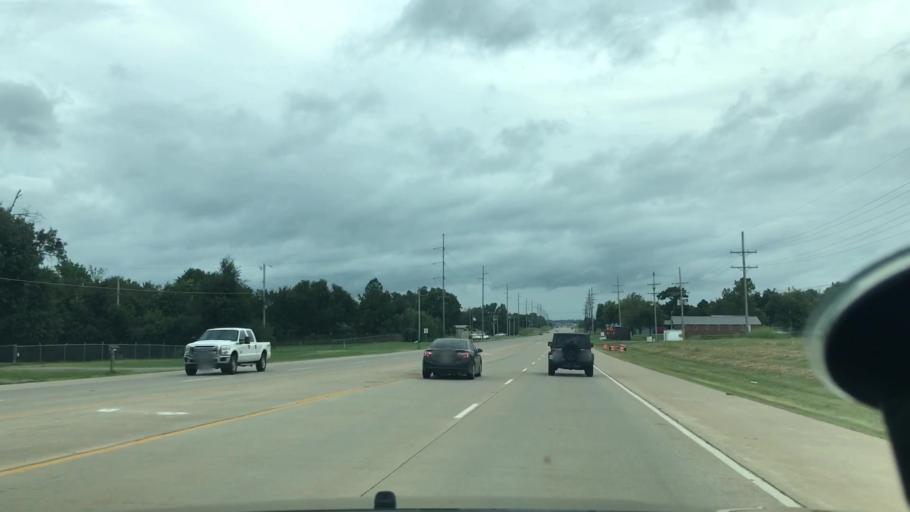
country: US
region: Oklahoma
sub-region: Seminole County
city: Seminole
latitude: 35.2632
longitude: -96.6711
